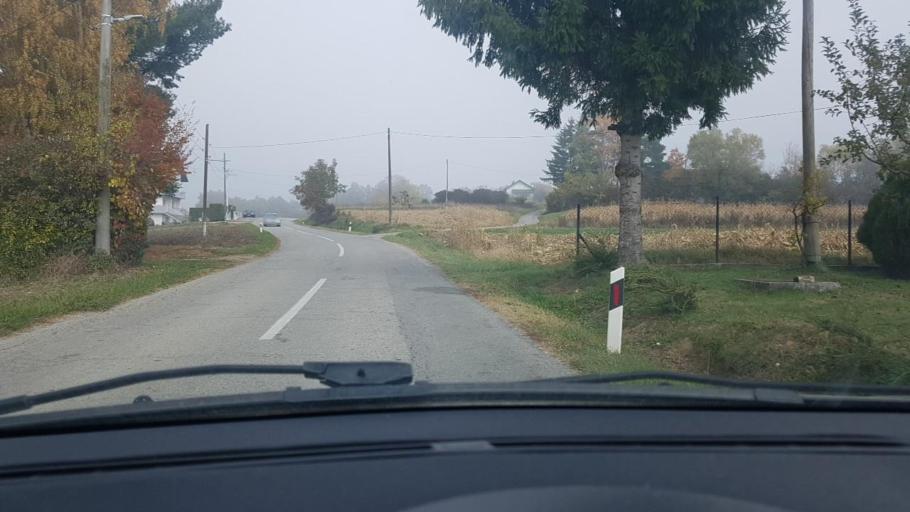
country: HR
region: Krapinsko-Zagorska
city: Zlatar
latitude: 46.1236
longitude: 16.1154
